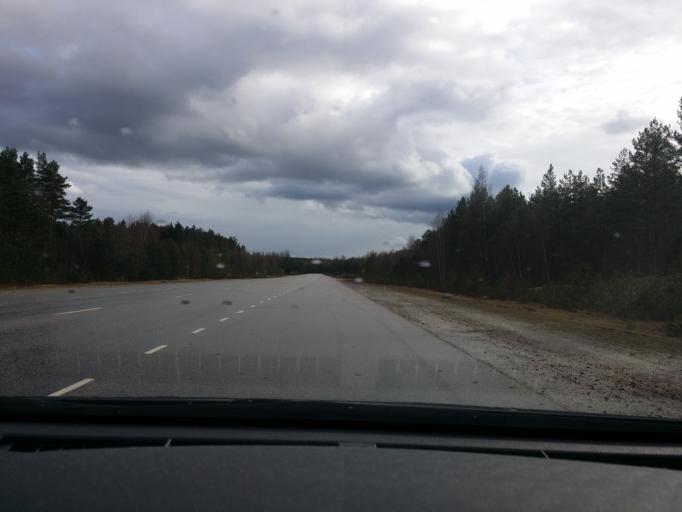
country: SE
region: Soedermanland
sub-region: Eskilstuna Kommun
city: Arla
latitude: 59.3262
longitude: 16.6823
